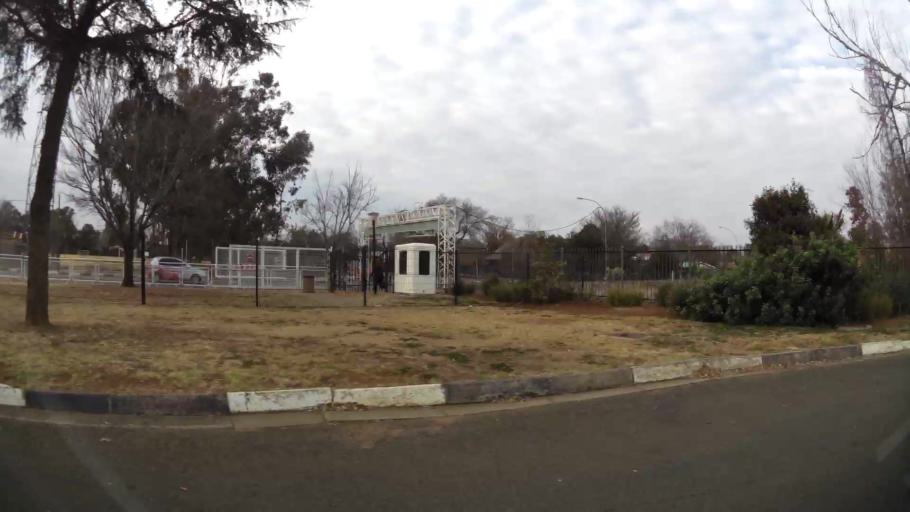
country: ZA
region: Orange Free State
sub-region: Mangaung Metropolitan Municipality
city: Bloemfontein
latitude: -29.1161
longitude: 26.1905
